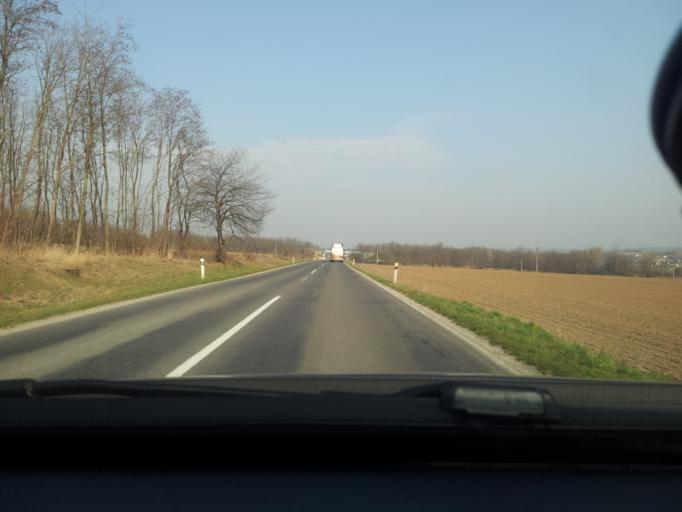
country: SK
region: Trnavsky
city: Hlohovec
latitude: 48.3785
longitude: 17.8761
